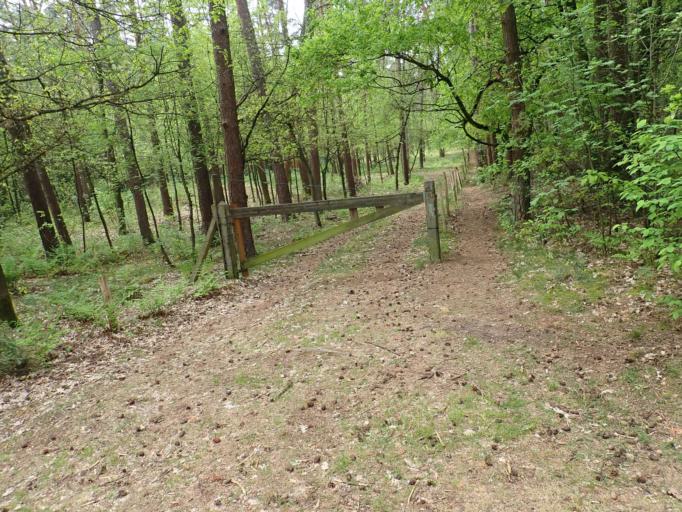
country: BE
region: Flanders
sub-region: Provincie Antwerpen
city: Herentals
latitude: 51.2031
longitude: 4.8469
